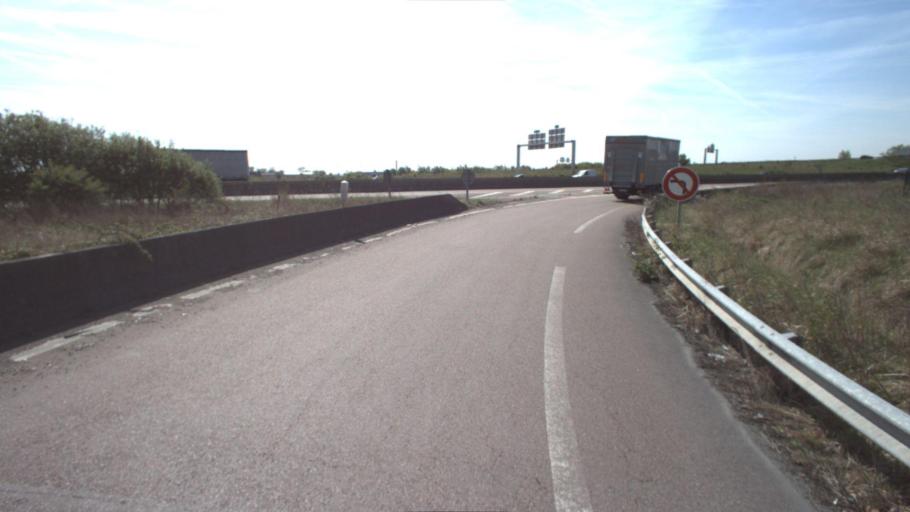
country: FR
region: Ile-de-France
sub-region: Departement de Seine-et-Marne
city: Mitry-Mory
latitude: 49.0022
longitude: 2.6391
